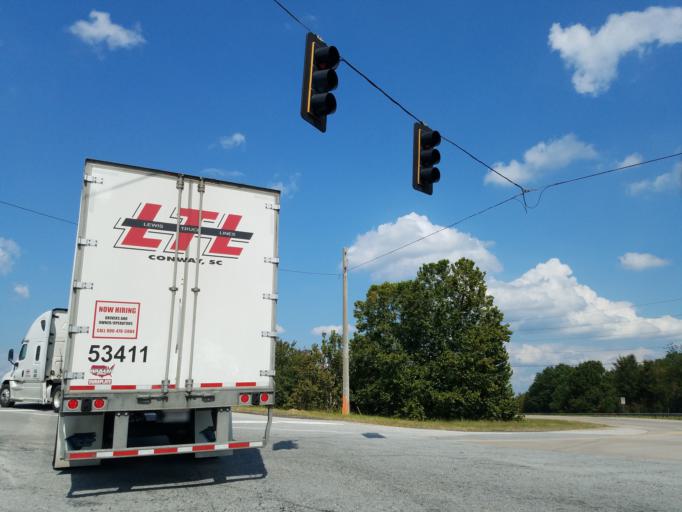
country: US
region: Georgia
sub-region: Jackson County
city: Braselton
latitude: 34.1167
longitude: -83.7623
